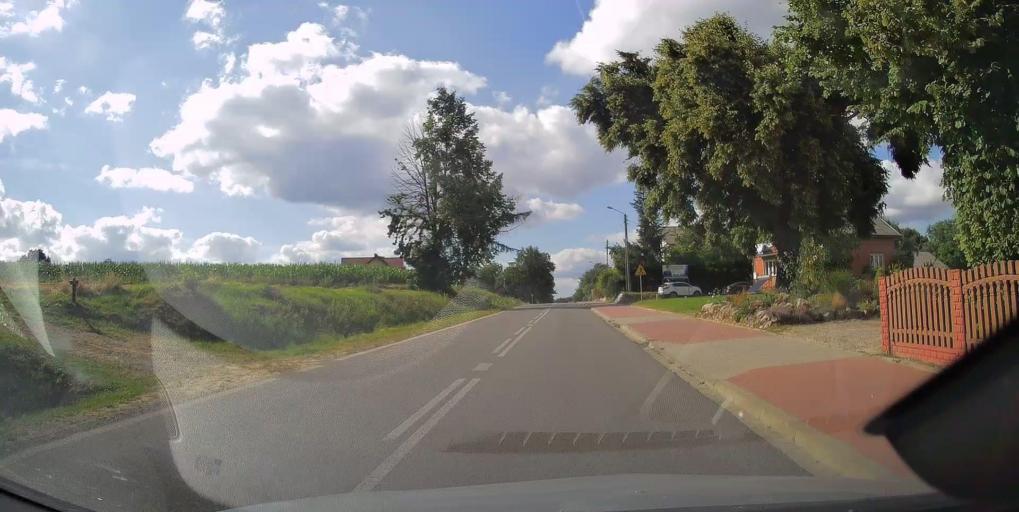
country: PL
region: Swietokrzyskie
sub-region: Powiat kielecki
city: Nowa Slupia
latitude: 50.8742
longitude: 21.0714
